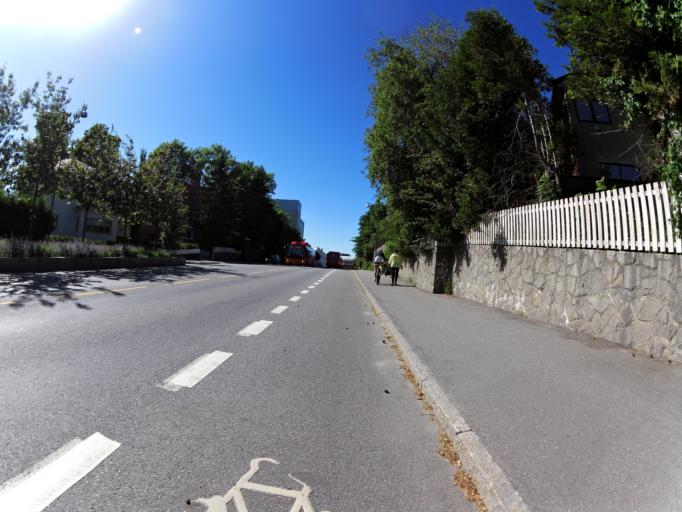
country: NO
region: Ostfold
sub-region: Fredrikstad
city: Fredrikstad
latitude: 59.2110
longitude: 10.9426
